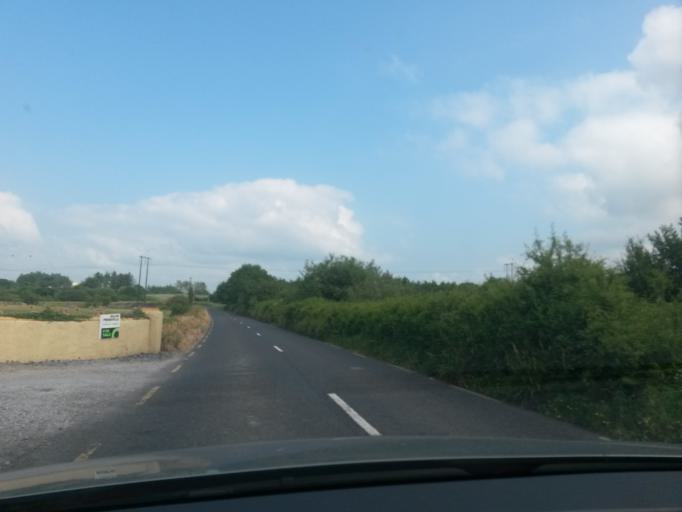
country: IE
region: Munster
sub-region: An Clar
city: Kilrush
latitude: 52.5636
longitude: -9.3959
